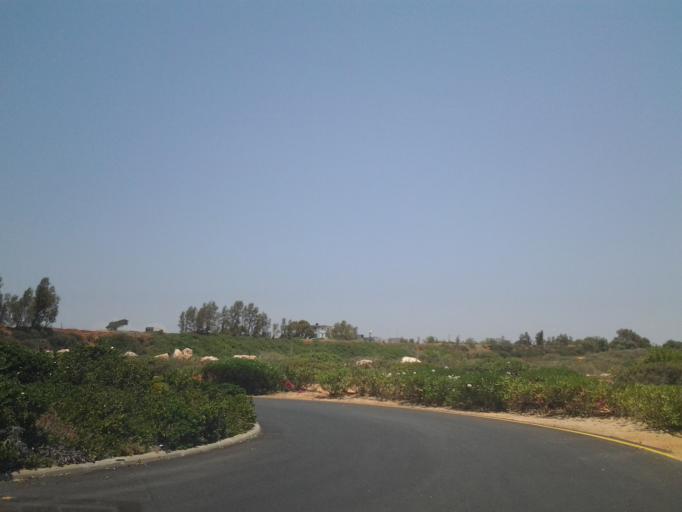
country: IL
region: Haifa
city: Qesarya
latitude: 32.5300
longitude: 34.9075
